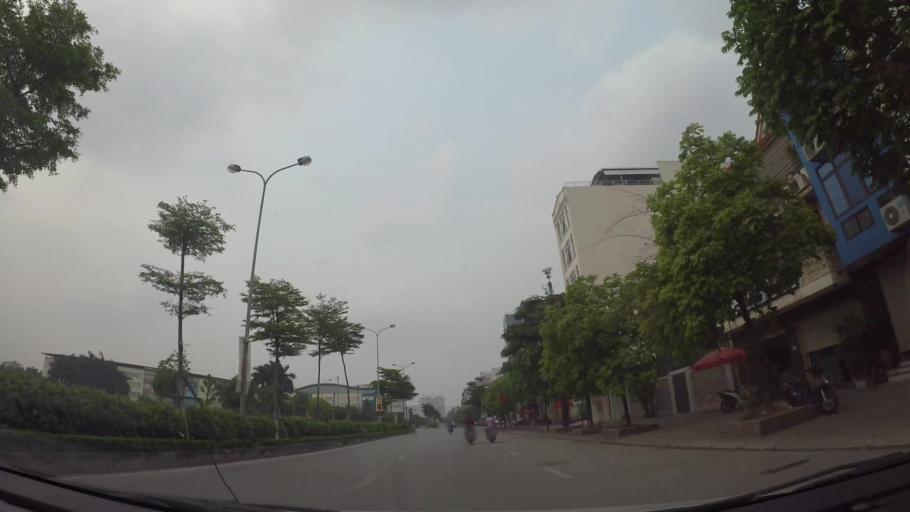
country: VN
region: Ha Noi
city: Cau Dien
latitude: 21.0417
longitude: 105.7735
